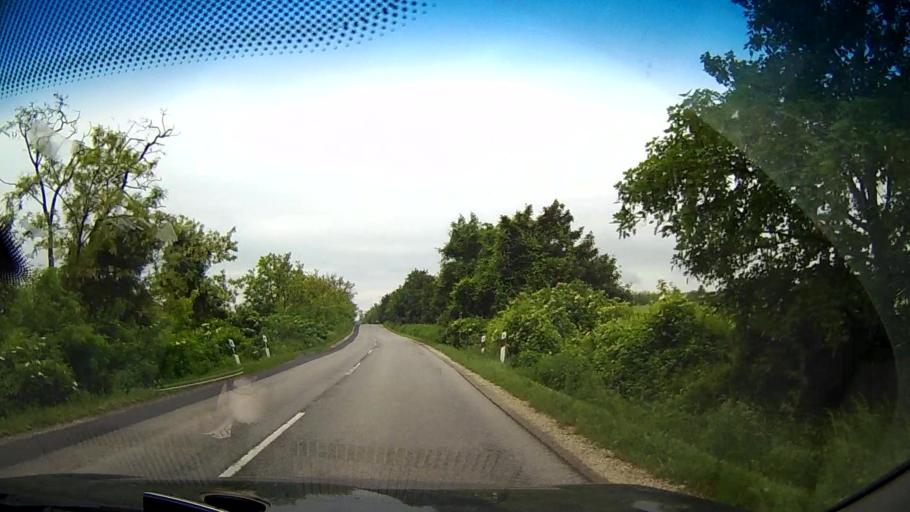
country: HU
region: Pest
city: Perbal
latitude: 47.5785
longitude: 18.7430
